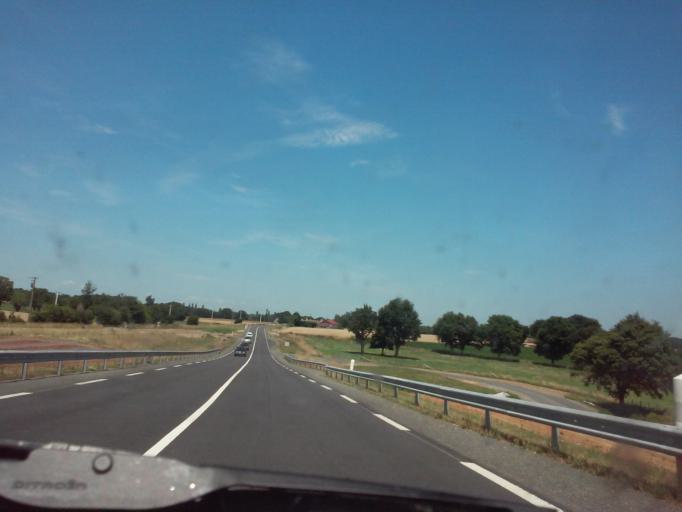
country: FR
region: Pays de la Loire
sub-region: Departement de la Sarthe
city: Beaufay
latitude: 48.0955
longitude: 0.3203
